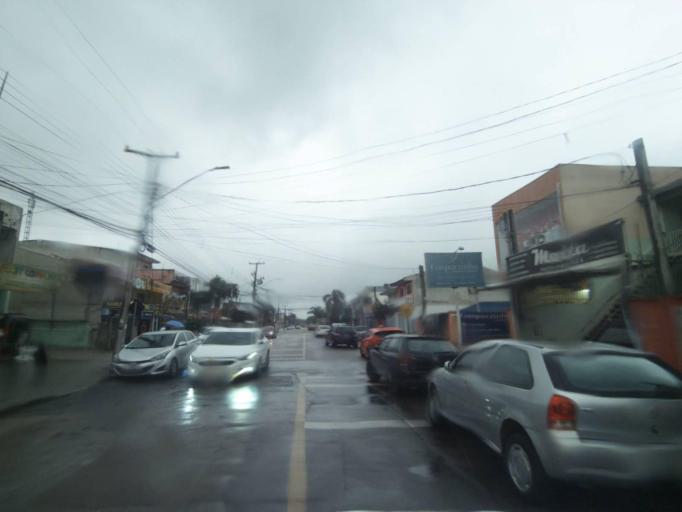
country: BR
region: Parana
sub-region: Araucaria
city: Araucaria
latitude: -25.5451
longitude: -49.3419
